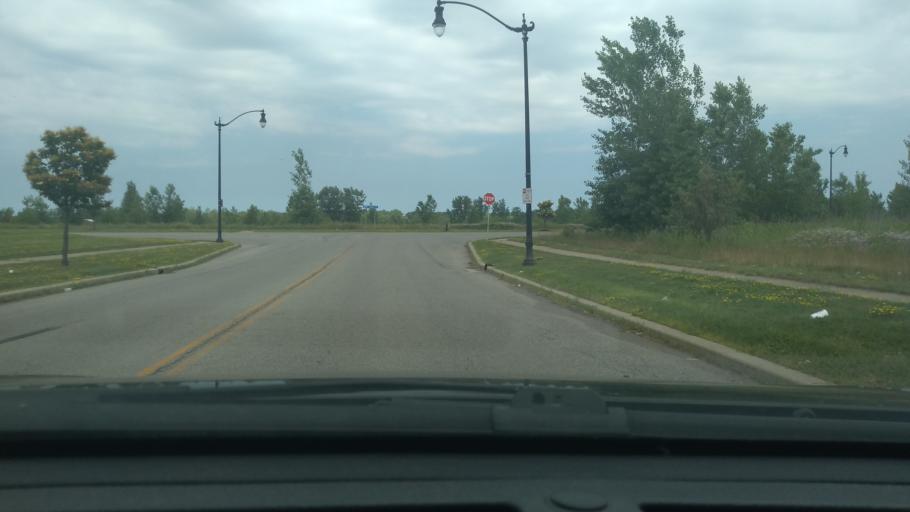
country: US
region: New York
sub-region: Erie County
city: Lackawanna
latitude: 42.8329
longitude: -78.8474
